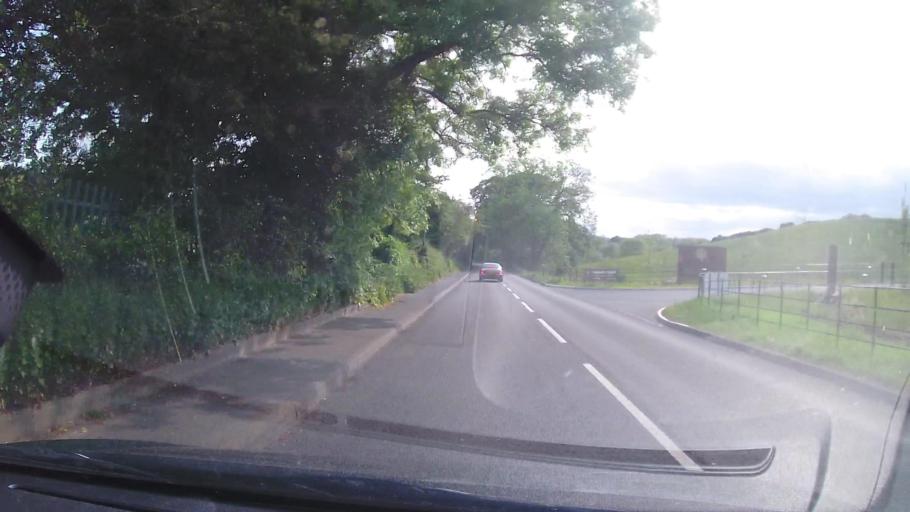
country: GB
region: England
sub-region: Shropshire
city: Shrewsbury
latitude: 52.7328
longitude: -2.7478
